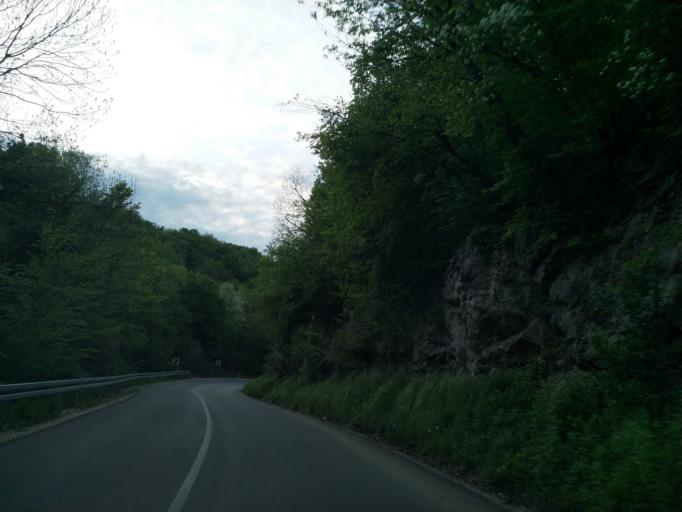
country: RS
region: Central Serbia
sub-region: Pomoravski Okrug
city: Despotovac
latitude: 43.9704
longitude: 21.5251
